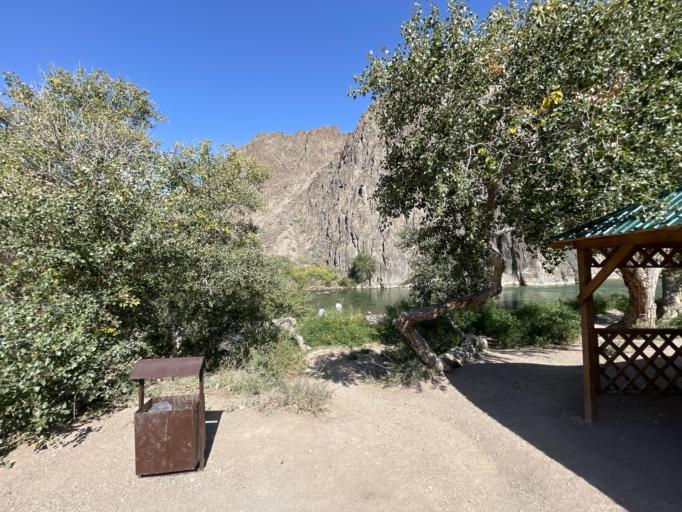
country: KZ
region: Almaty Oblysy
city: Kegen
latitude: 43.3507
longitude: 79.0814
